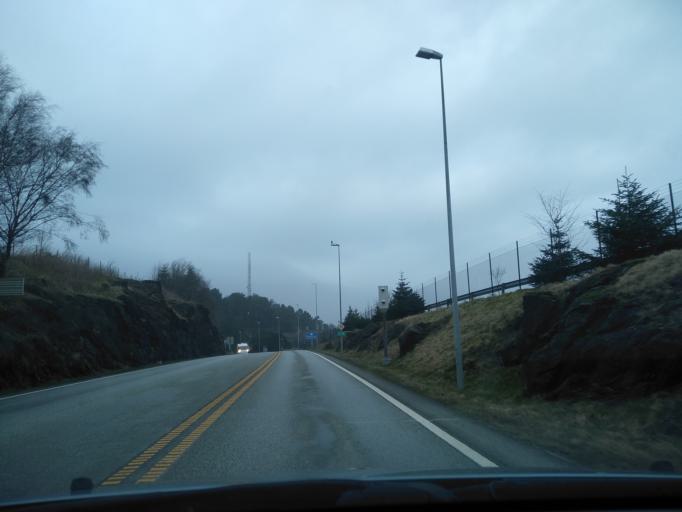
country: NO
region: Rogaland
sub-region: Randaberg
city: Randaberg
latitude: 59.0141
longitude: 5.6344
